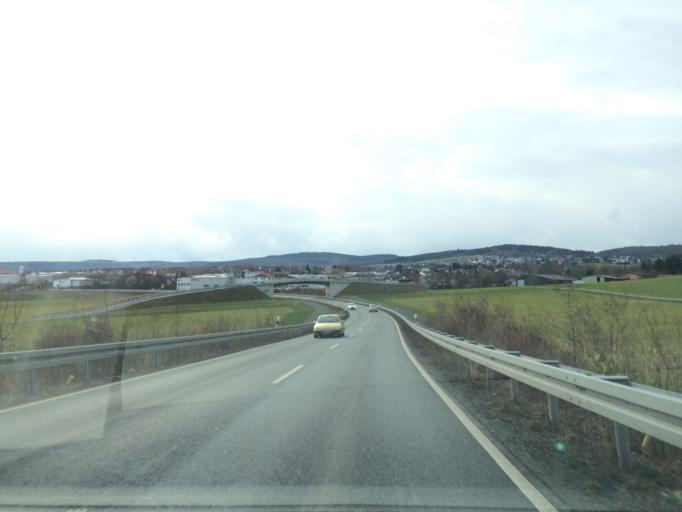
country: DE
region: Hesse
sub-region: Regierungsbezirk Darmstadt
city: Neu-Anspach
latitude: 50.3133
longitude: 8.5137
